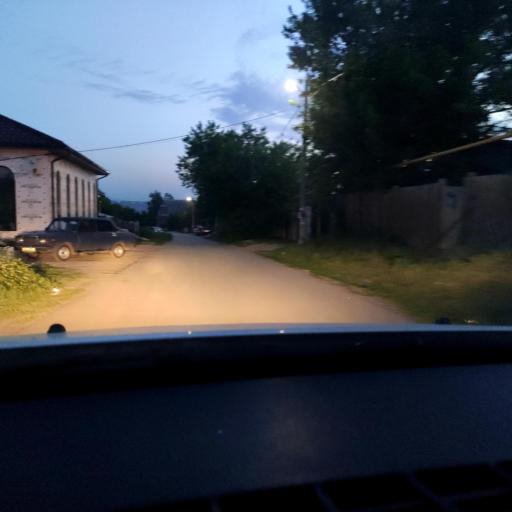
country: RU
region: Voronezj
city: Podgornoye
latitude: 51.8008
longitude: 39.1399
